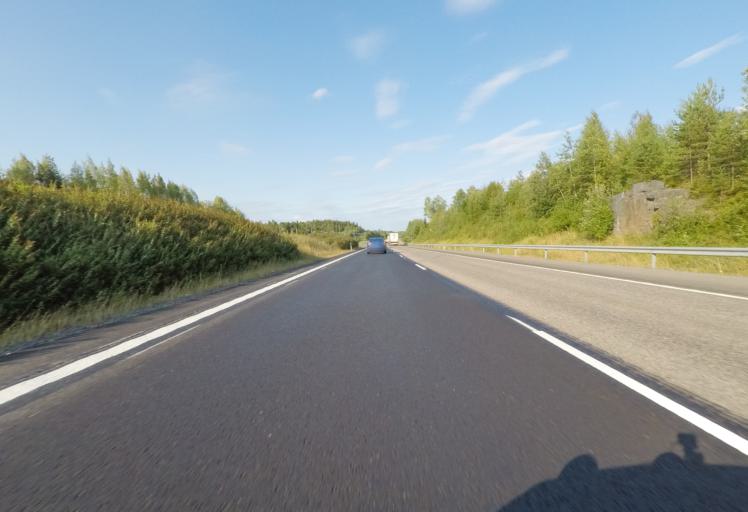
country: FI
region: Uusimaa
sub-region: Helsinki
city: Maentsaelae
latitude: 60.7005
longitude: 25.4056
